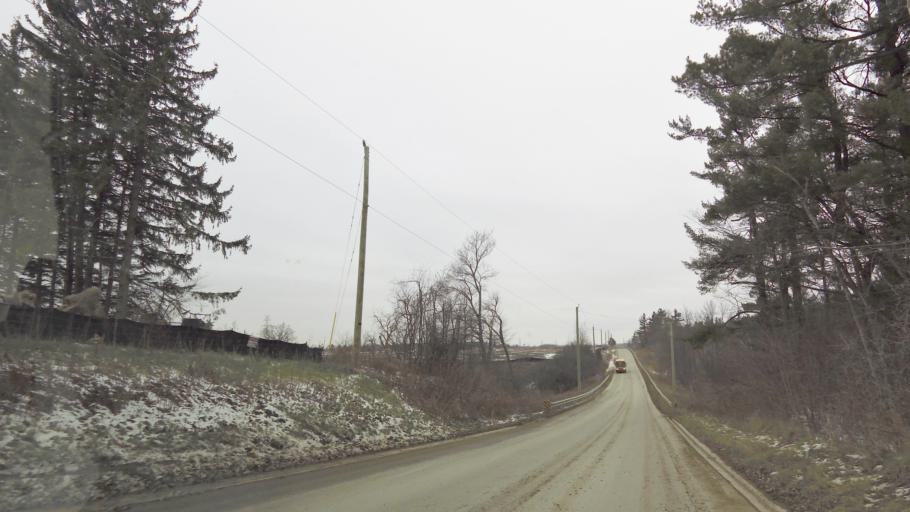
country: CA
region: Ontario
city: Vaughan
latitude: 43.8582
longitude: -79.6158
